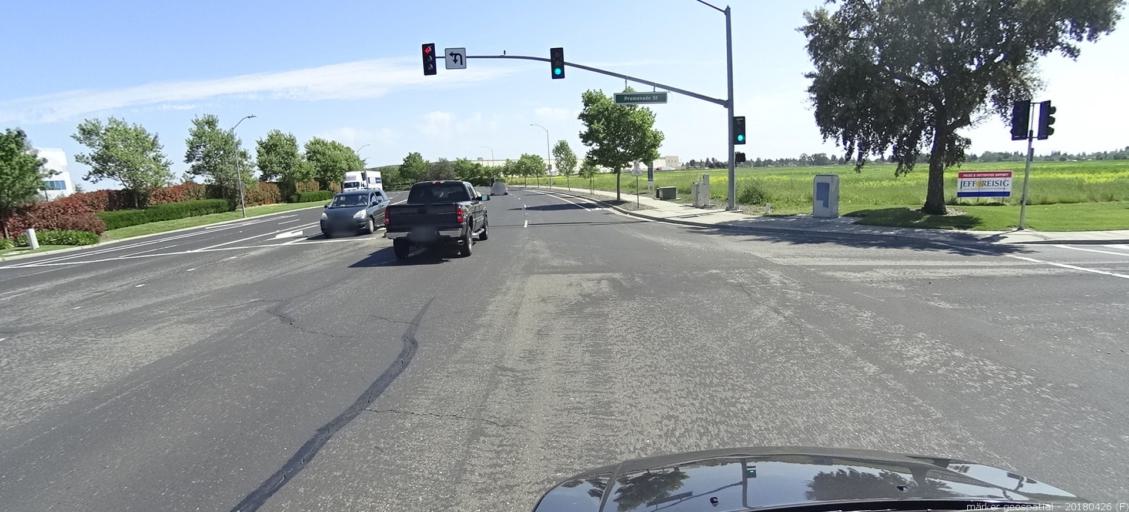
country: US
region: California
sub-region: Yolo County
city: West Sacramento
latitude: 38.5455
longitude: -121.5686
